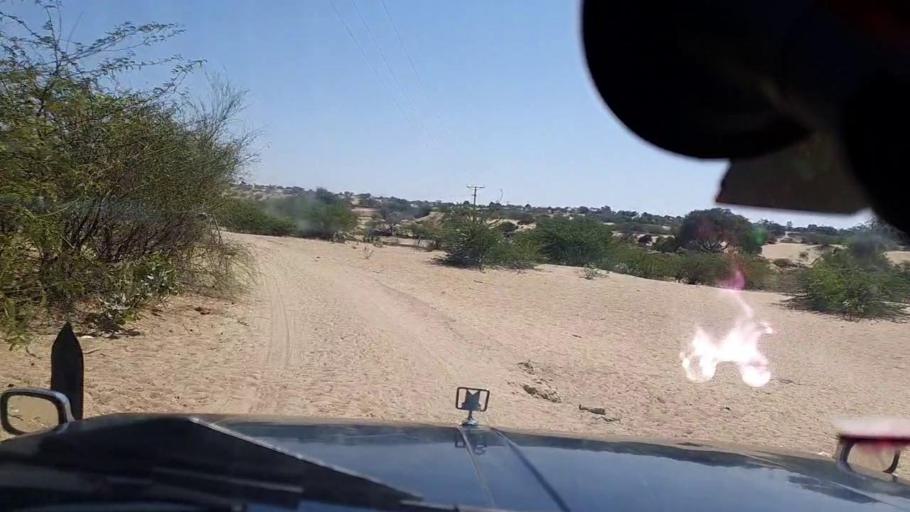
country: PK
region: Sindh
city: Diplo
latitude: 24.5666
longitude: 69.6831
